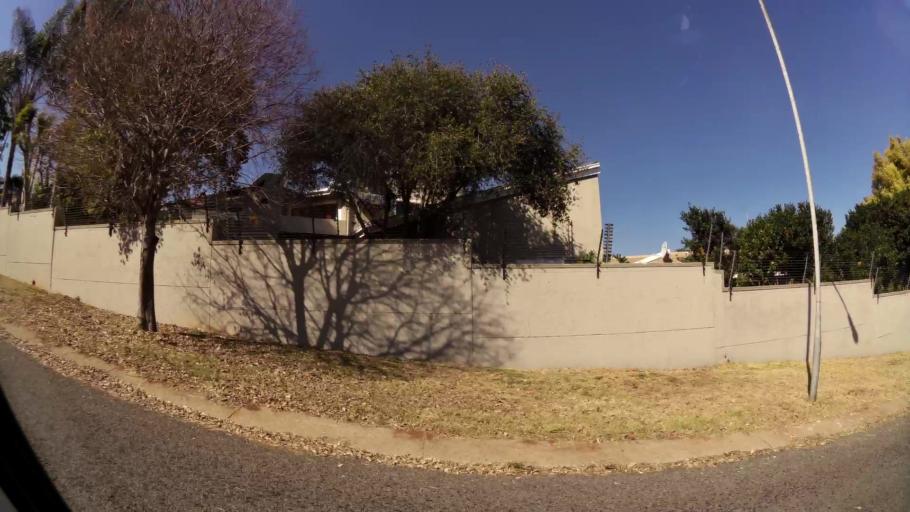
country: ZA
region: Gauteng
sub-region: City of Tshwane Metropolitan Municipality
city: Pretoria
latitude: -25.7966
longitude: 28.2279
